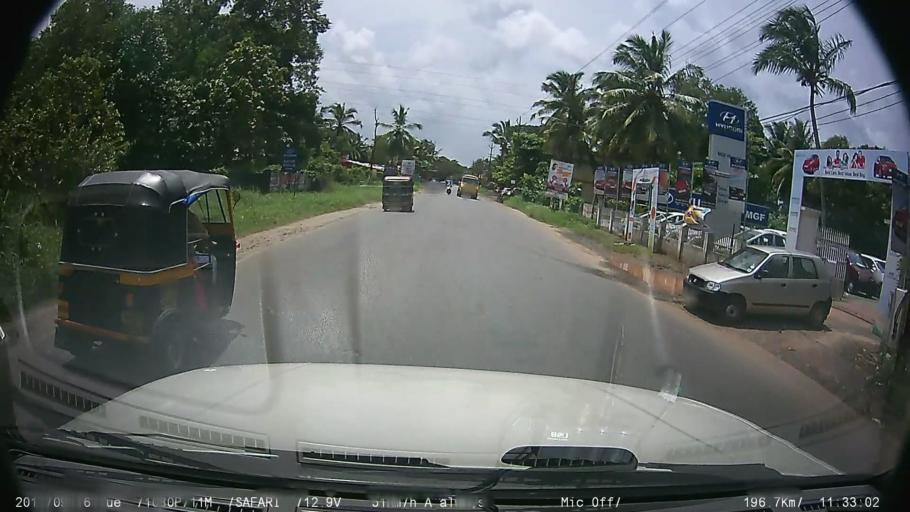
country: IN
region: Kerala
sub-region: Kottayam
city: Changanacheri
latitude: 9.4700
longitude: 76.5293
